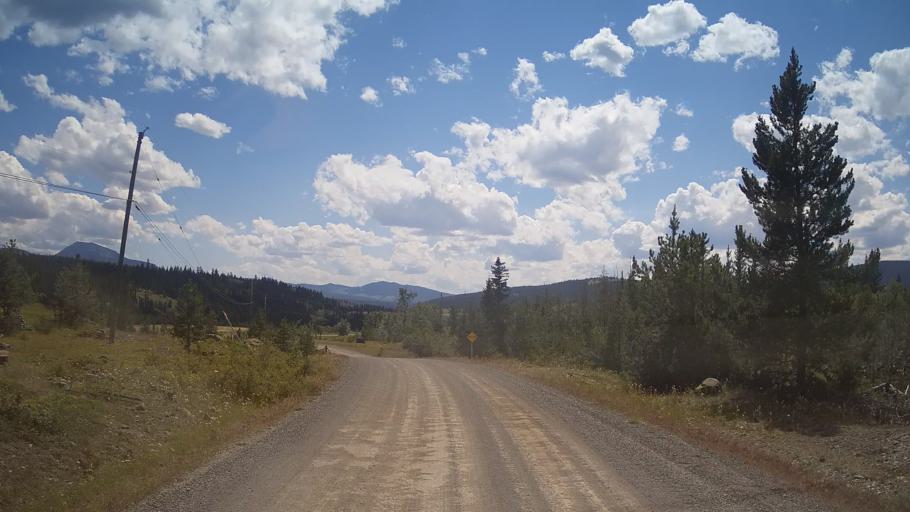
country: CA
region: British Columbia
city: Lillooet
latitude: 51.3317
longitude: -121.9756
